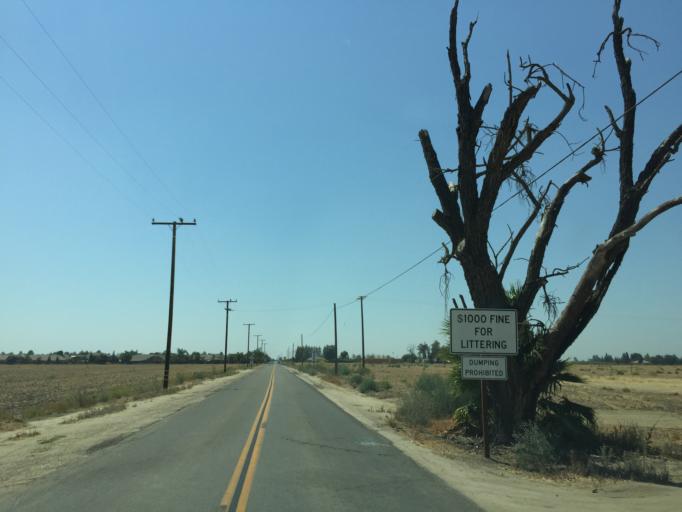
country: US
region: California
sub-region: Tulare County
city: Visalia
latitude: 36.3655
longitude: -119.3147
